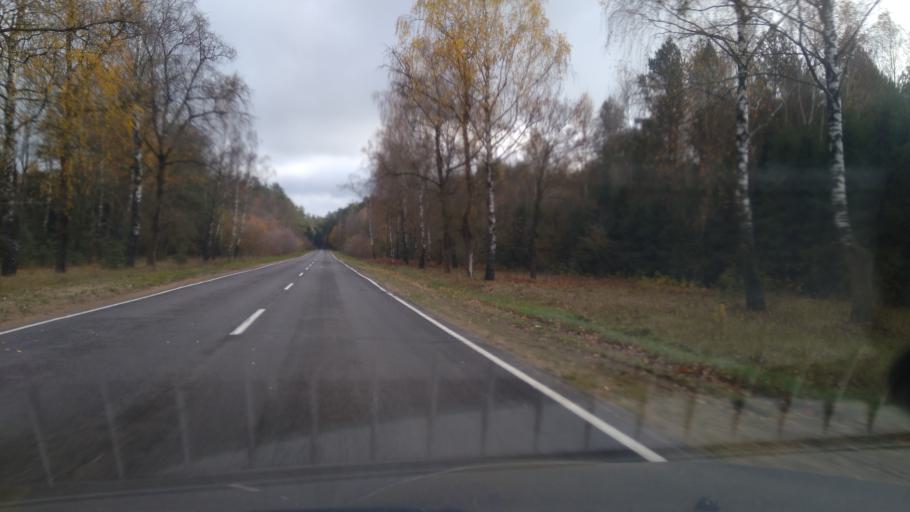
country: BY
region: Minsk
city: Slutsk
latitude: 53.2195
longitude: 27.5686
